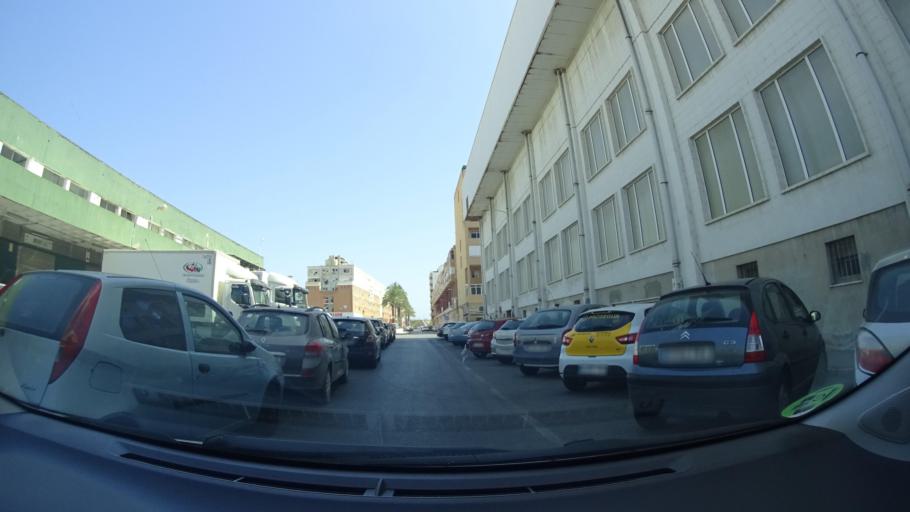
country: ES
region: Andalusia
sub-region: Provincia de Cadiz
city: Cadiz
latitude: 36.4981
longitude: -6.2707
